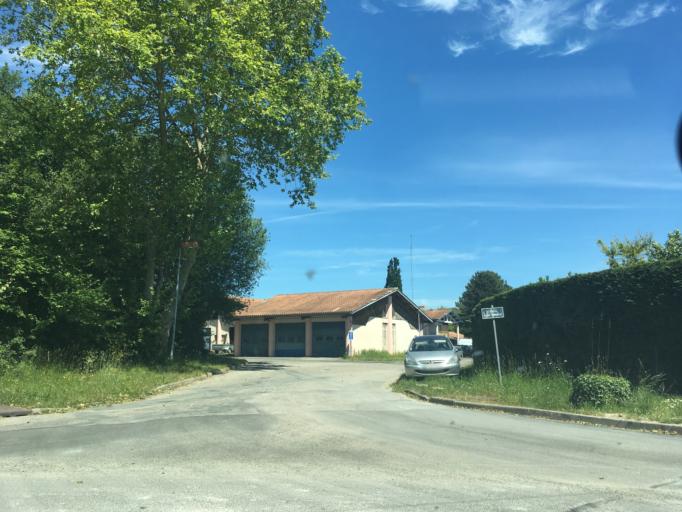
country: FR
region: Aquitaine
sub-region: Departement de la Gironde
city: Castelnau-de-Medoc
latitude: 45.0365
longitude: -0.8018
